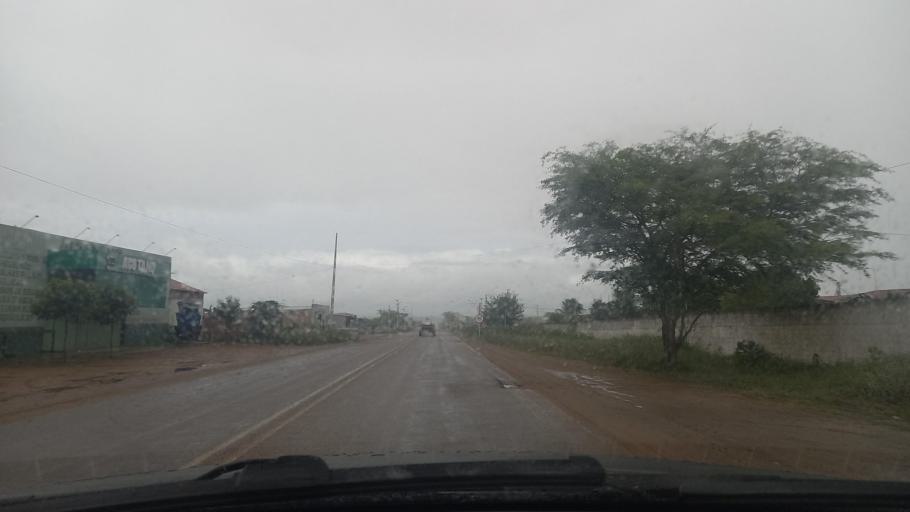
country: BR
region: Bahia
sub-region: Paulo Afonso
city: Paulo Afonso
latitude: -9.3587
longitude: -38.2760
